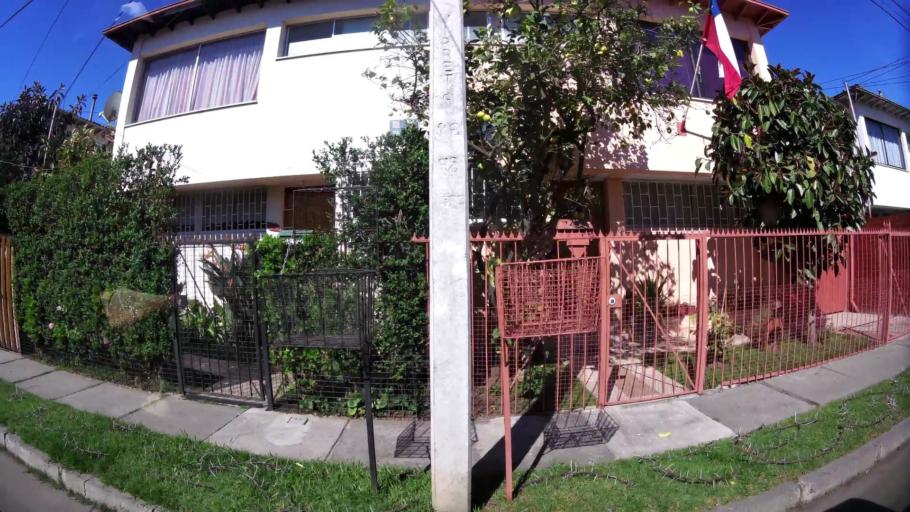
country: CL
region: Santiago Metropolitan
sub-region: Provincia de Talagante
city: Penaflor
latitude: -33.6058
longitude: -70.9035
